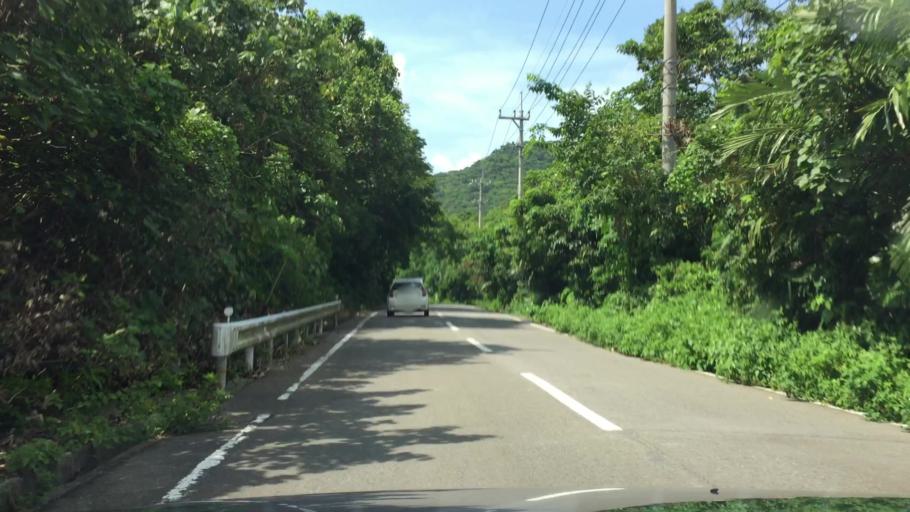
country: JP
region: Okinawa
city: Ishigaki
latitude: 24.4640
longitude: 124.2268
